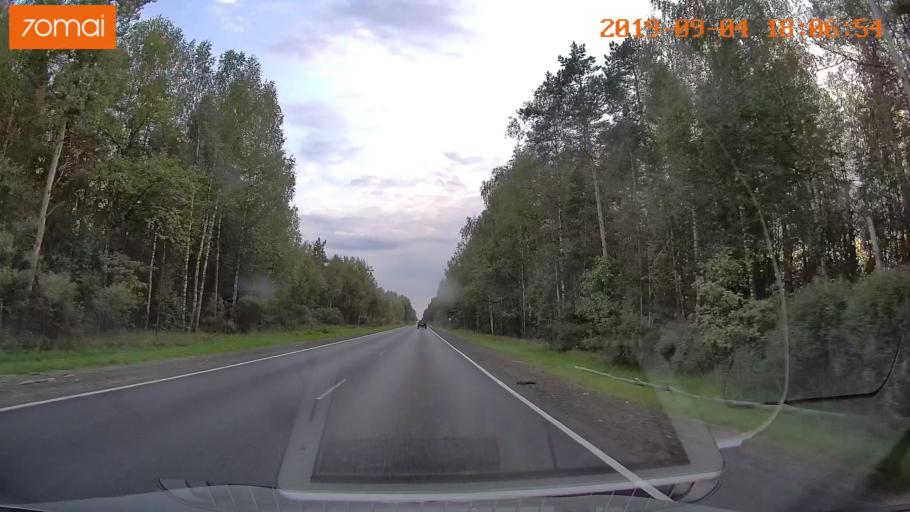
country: RU
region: Moskovskaya
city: Khorlovo
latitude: 55.4260
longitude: 38.8088
